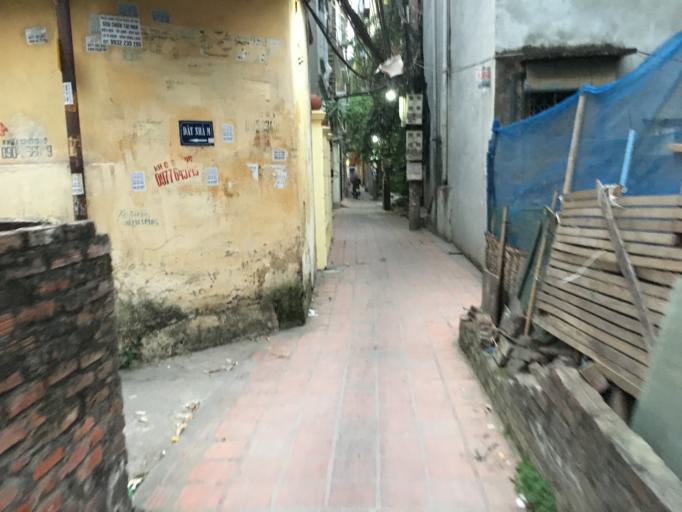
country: VN
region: Ha Noi
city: Cau Giay
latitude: 21.0476
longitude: 105.7877
